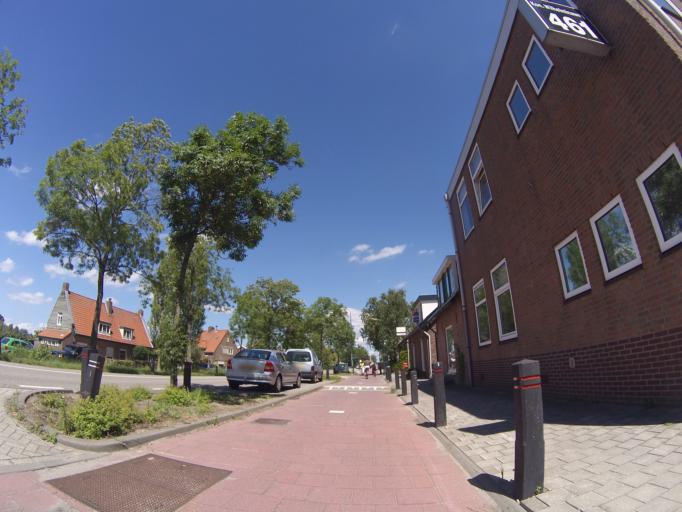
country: NL
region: Utrecht
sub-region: Gemeente Utrecht
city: Utrecht
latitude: 52.1239
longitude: 5.1435
